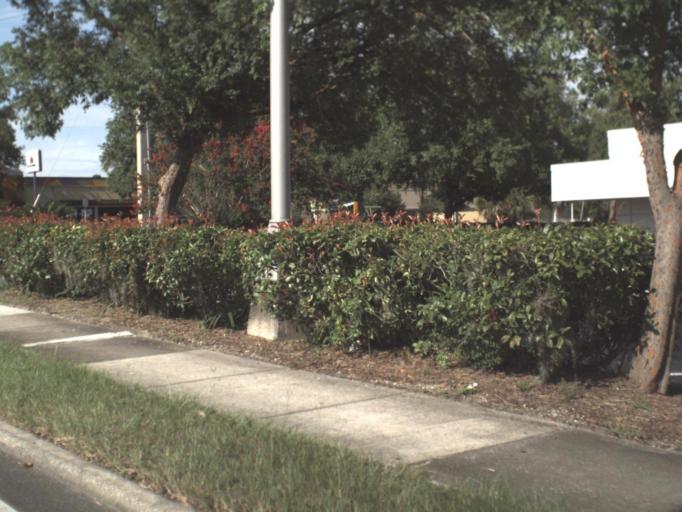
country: US
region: Florida
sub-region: Alachua County
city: Gainesville
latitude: 29.6744
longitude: -82.3392
